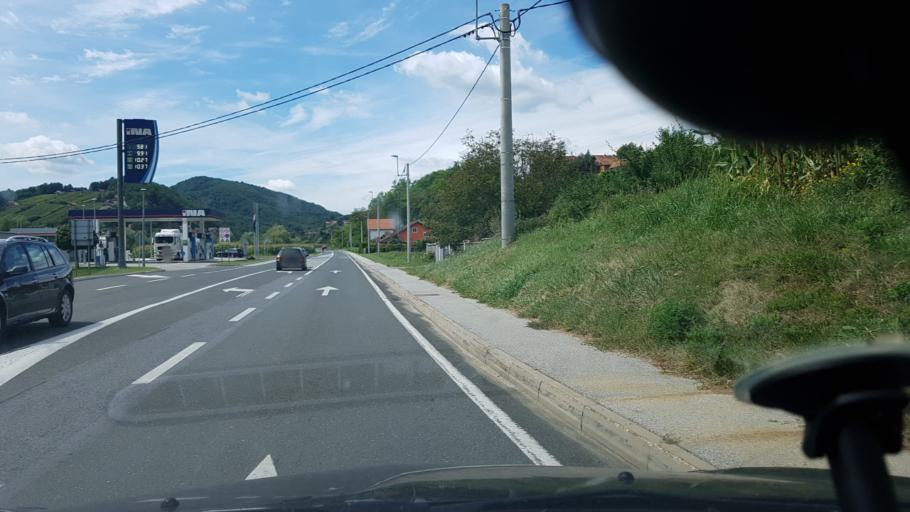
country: HR
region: Varazdinska
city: Lepoglava
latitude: 46.2072
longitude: 16.0322
